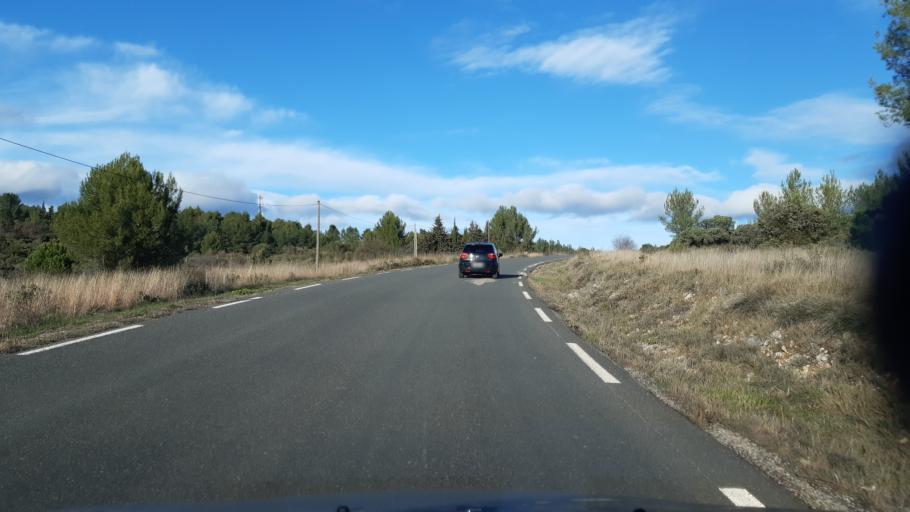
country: FR
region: Languedoc-Roussillon
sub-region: Departement de l'Herault
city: Murviel-les-Montpellier
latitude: 43.6307
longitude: 3.7460
